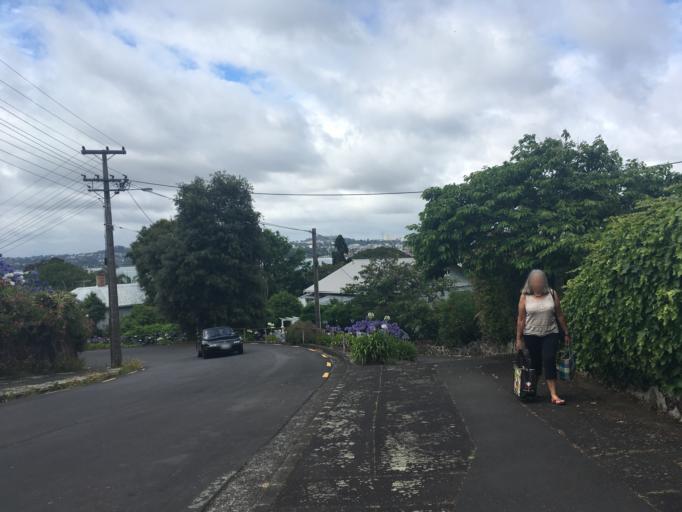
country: NZ
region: Auckland
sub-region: Auckland
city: Auckland
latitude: -36.8292
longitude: 174.8005
